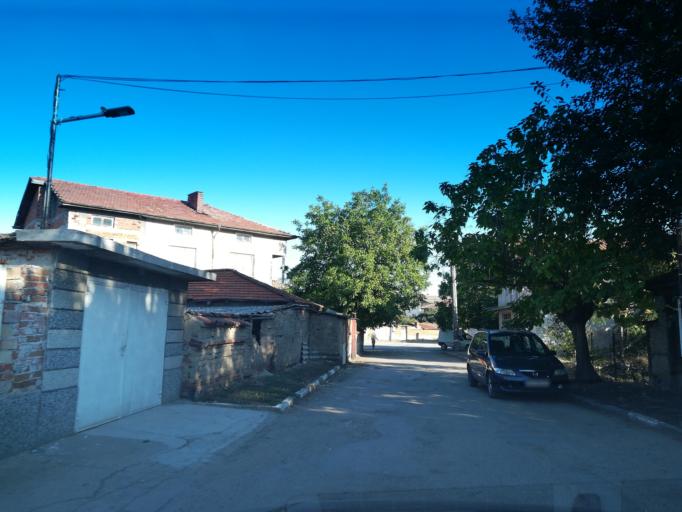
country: BG
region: Stara Zagora
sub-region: Obshtina Chirpan
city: Chirpan
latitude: 42.1063
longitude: 25.2190
